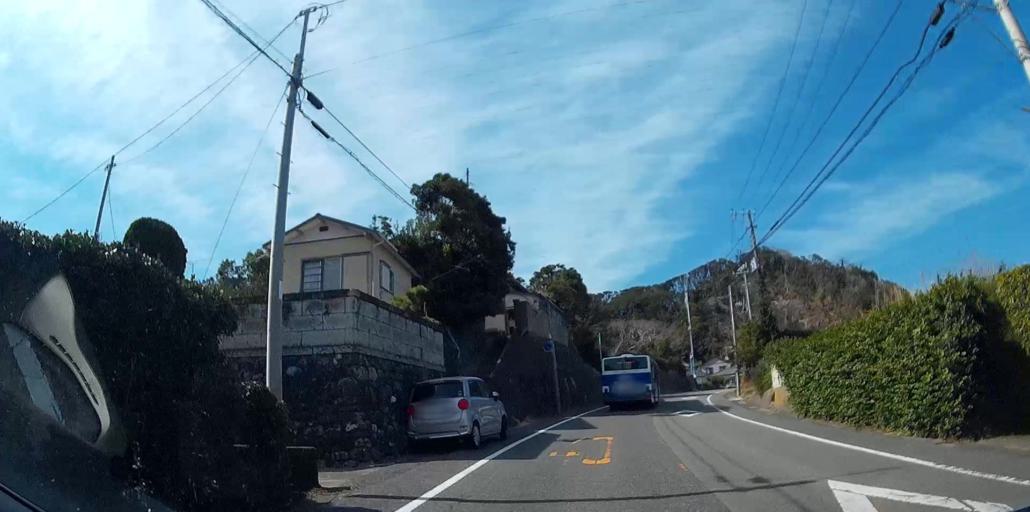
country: JP
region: Chiba
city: Tateyama
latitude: 34.9729
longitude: 139.7829
